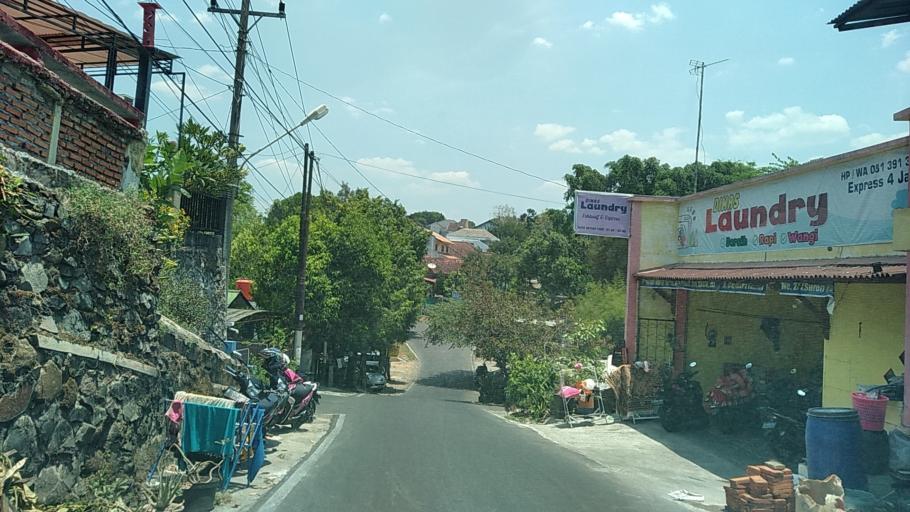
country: ID
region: Central Java
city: Ungaran
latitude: -7.0742
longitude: 110.4258
